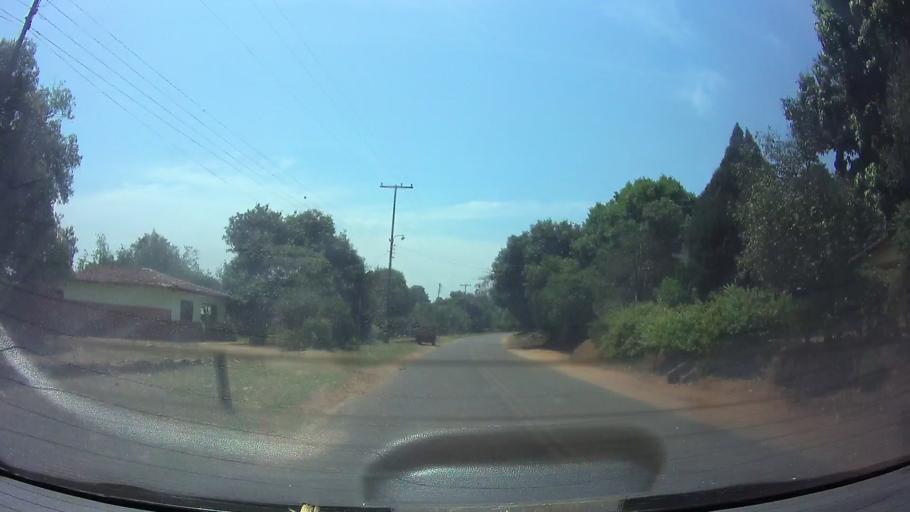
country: PY
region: Central
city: Ita
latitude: -25.4314
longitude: -57.3974
